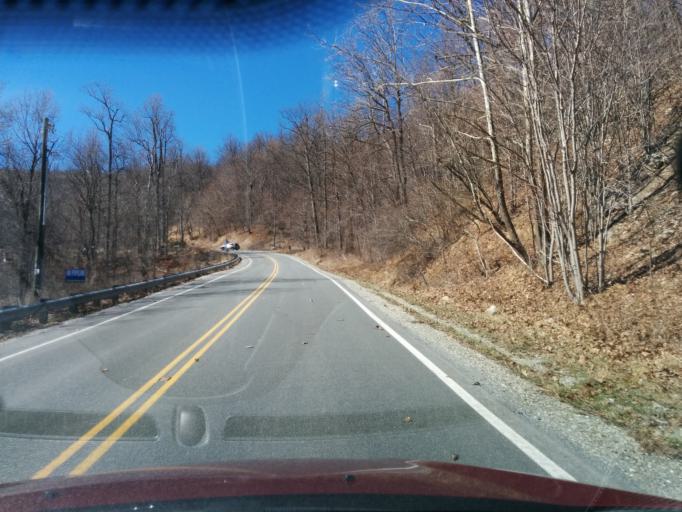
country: US
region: Virginia
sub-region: Nelson County
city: Nellysford
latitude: 37.9043
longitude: -78.9710
